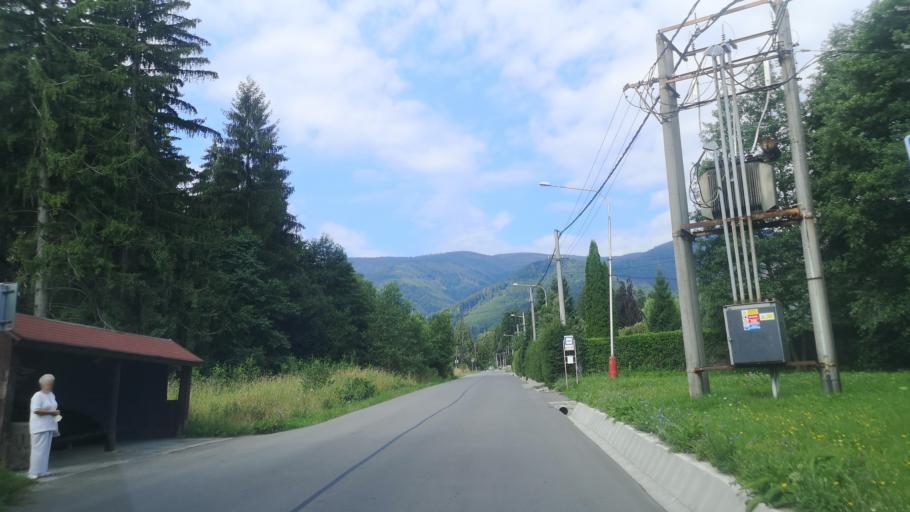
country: SK
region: Zilinsky
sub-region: Okres Martin
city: Martin
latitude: 49.0811
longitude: 18.8881
